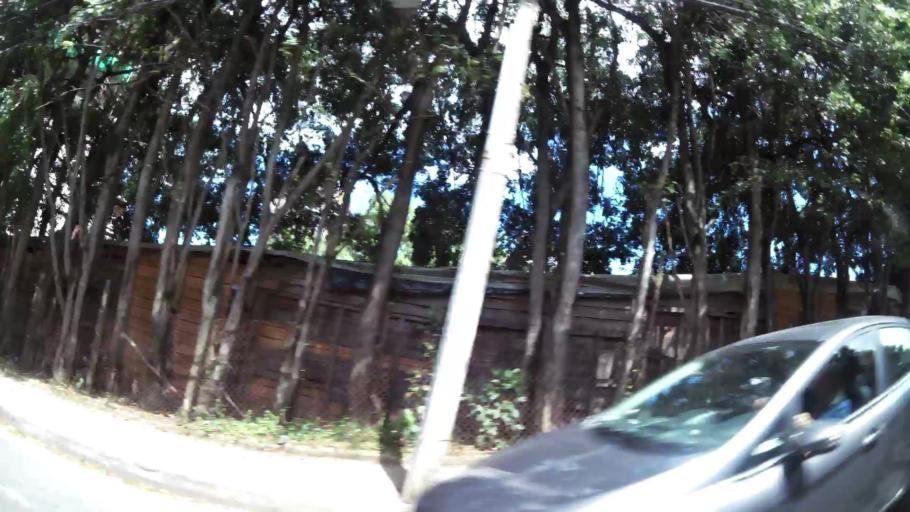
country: CO
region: Antioquia
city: Sabaneta
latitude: 6.1461
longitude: -75.6193
